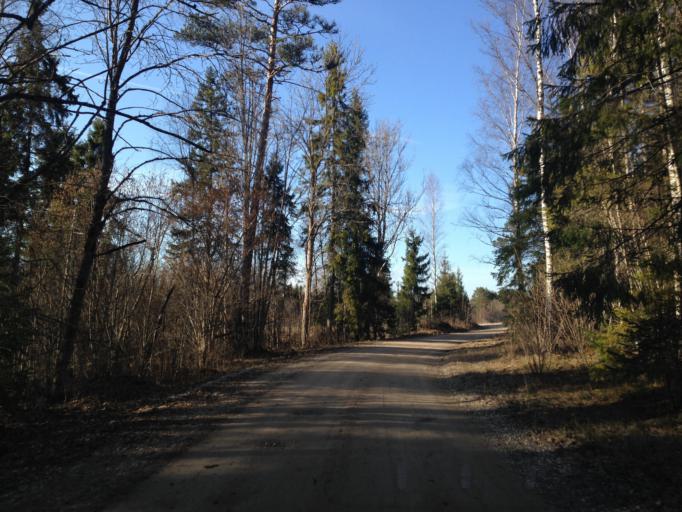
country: EE
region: Harju
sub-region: Nissi vald
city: Turba
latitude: 59.1274
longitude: 24.1663
